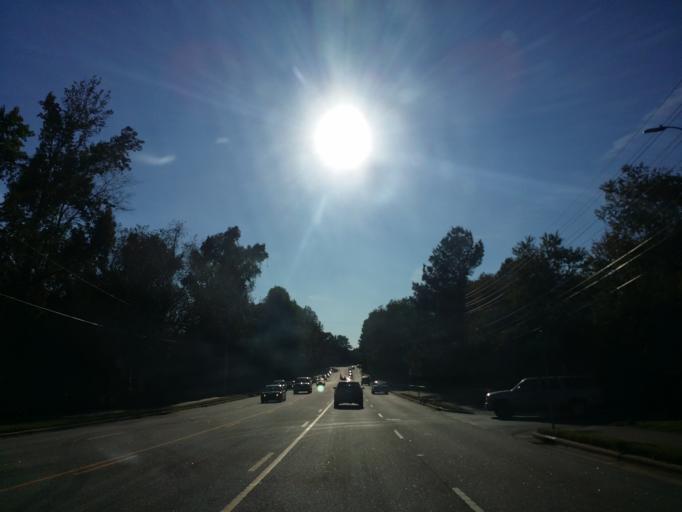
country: US
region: North Carolina
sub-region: Wake County
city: West Raleigh
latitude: 35.7706
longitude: -78.6884
